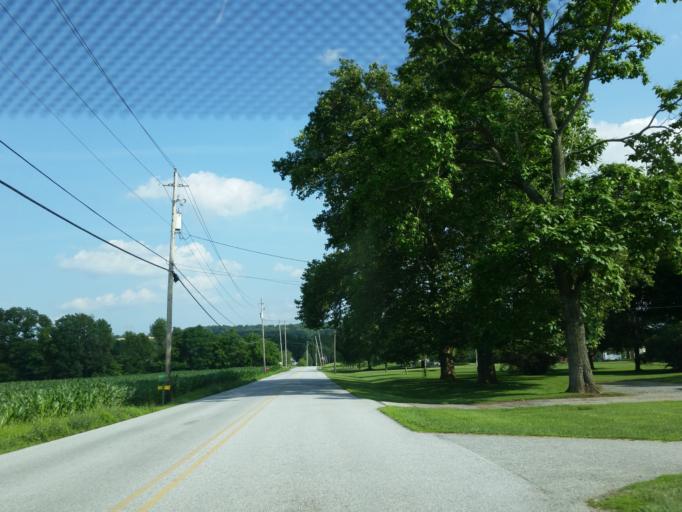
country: US
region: Pennsylvania
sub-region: York County
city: Stonybrook
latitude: 39.9931
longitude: -76.6285
